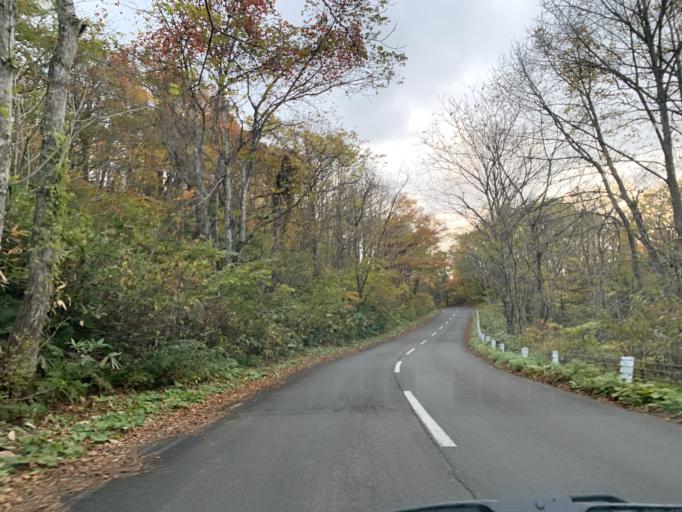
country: JP
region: Iwate
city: Mizusawa
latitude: 39.1068
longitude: 140.8728
